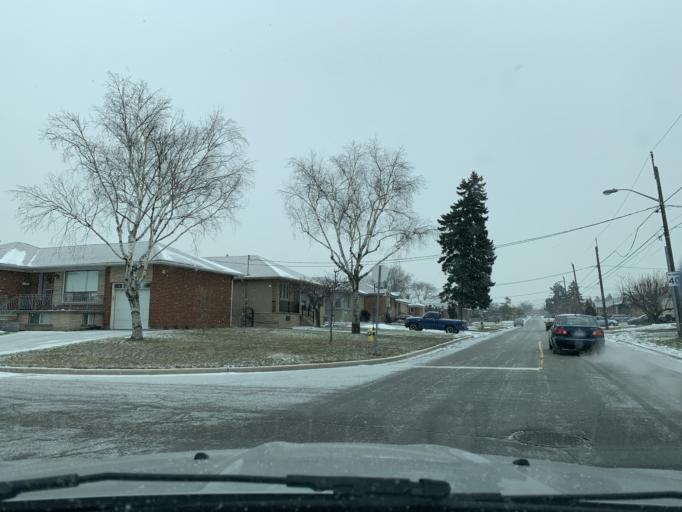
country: CA
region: Ontario
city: Concord
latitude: 43.7328
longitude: -79.4910
